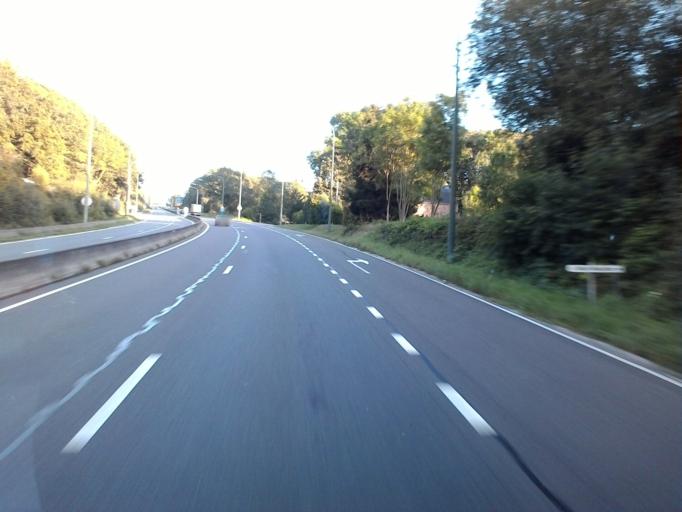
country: BE
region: Wallonia
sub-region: Province du Luxembourg
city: Marche-en-Famenne
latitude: 50.2182
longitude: 5.3448
